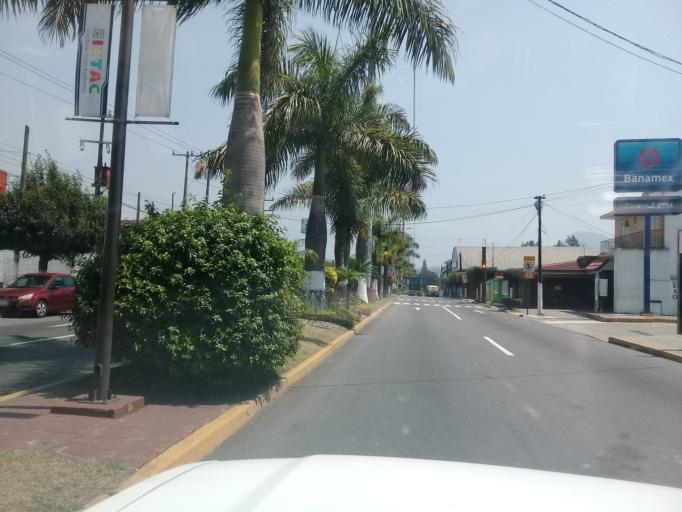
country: MX
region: Veracruz
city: Ixtac Zoquitlan
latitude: 18.8602
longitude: -97.0638
